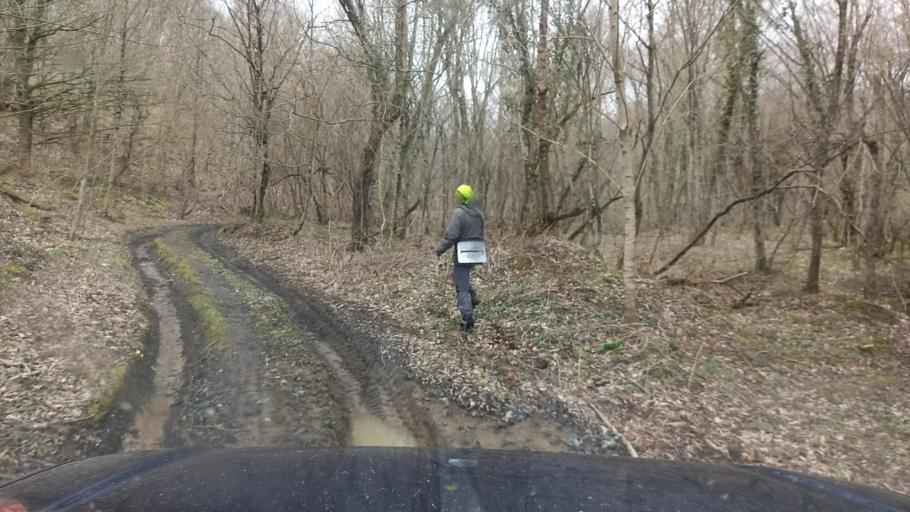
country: RU
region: Krasnodarskiy
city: Pshada
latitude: 44.4900
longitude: 38.3932
